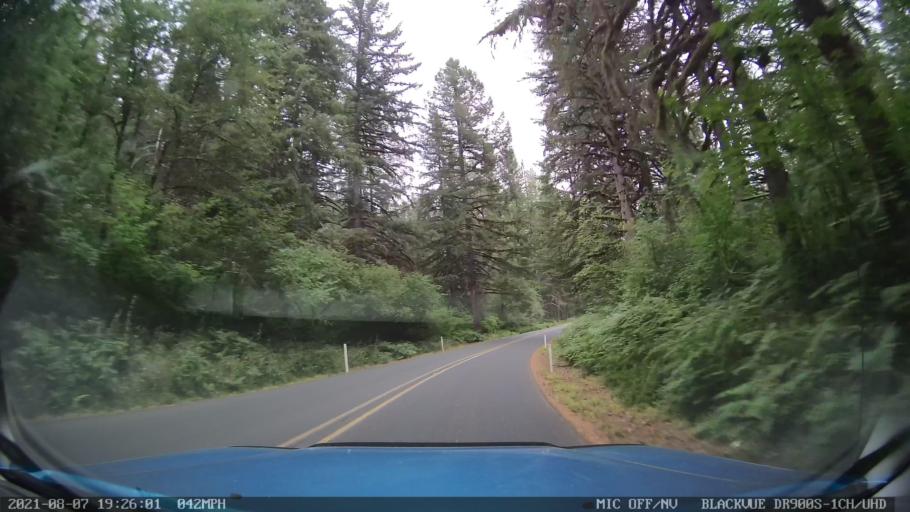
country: US
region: Oregon
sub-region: Linn County
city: Lyons
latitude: 44.8683
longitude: -122.6544
